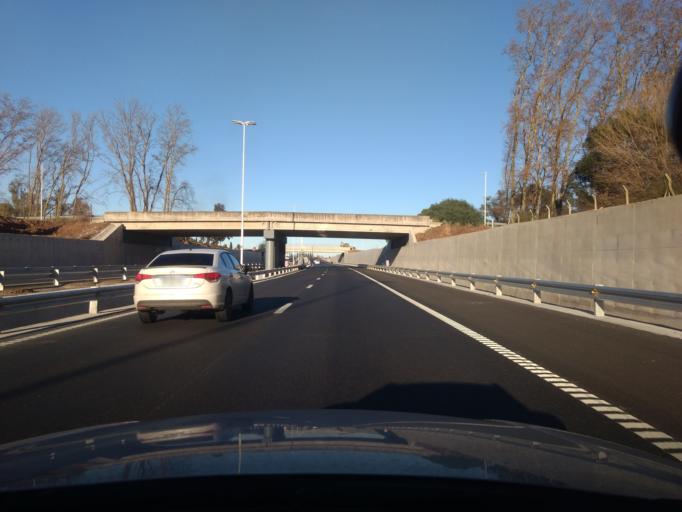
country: AR
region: Buenos Aires
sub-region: Partido de Lujan
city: Lujan
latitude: -34.5794
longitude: -59.0853
